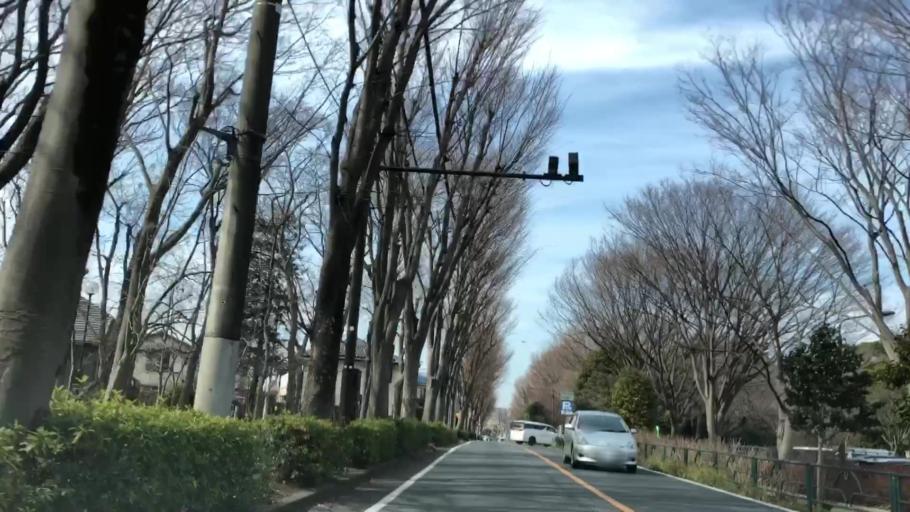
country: JP
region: Saitama
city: Wako
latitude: 35.7741
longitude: 139.5979
